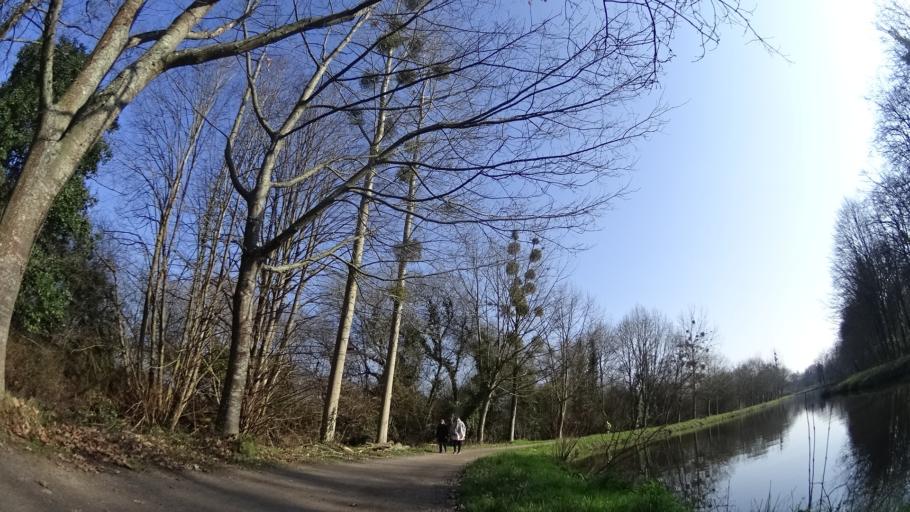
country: FR
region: Brittany
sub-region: Departement d'Ille-et-Vilaine
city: Saint-Gregoire
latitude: 48.1458
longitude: -1.6780
